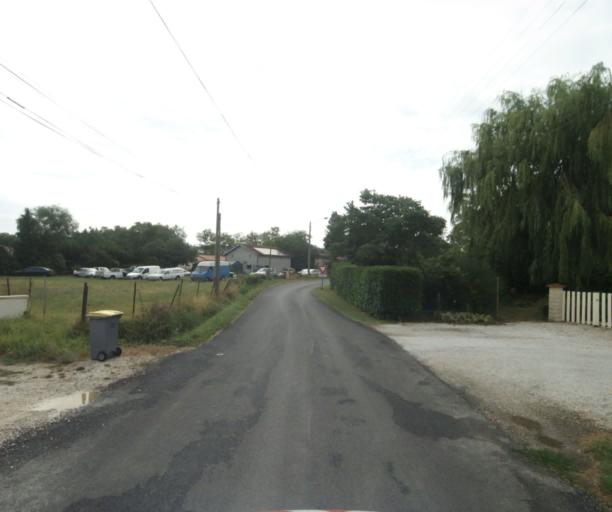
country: FR
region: Midi-Pyrenees
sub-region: Departement de la Haute-Garonne
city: Revel
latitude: 43.4504
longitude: 1.9693
